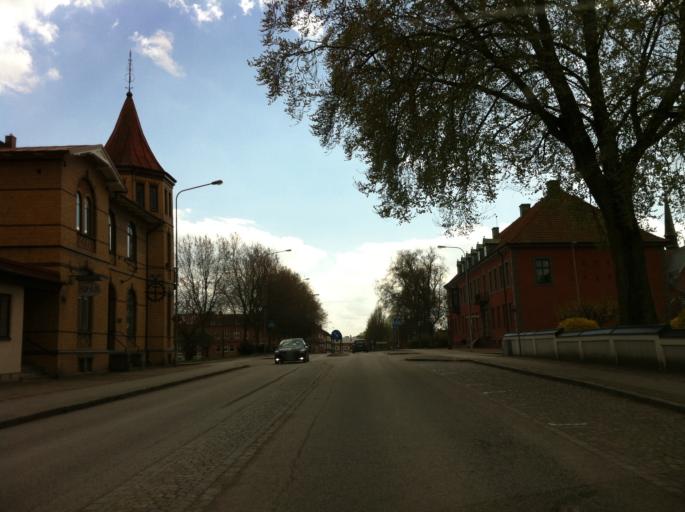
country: SE
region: Skane
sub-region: Eslovs Kommun
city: Eslov
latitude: 55.8365
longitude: 13.3001
